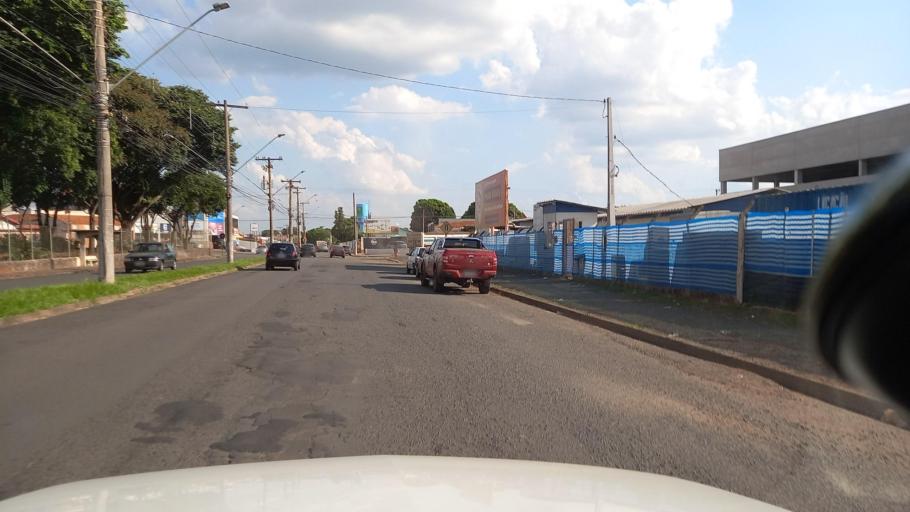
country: BR
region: Sao Paulo
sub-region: Moji-Guacu
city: Mogi-Gaucu
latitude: -22.3517
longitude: -46.9460
